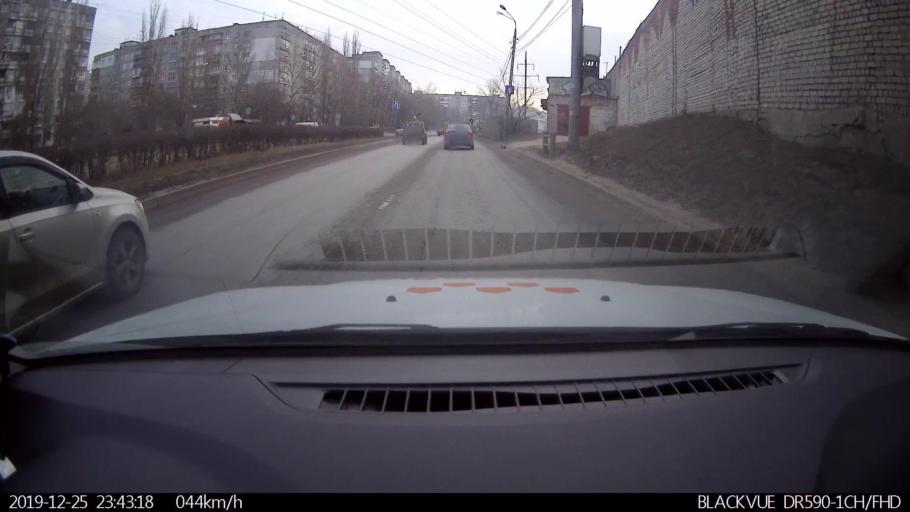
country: RU
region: Nizjnij Novgorod
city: Nizhniy Novgorod
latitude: 56.3370
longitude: 43.9259
